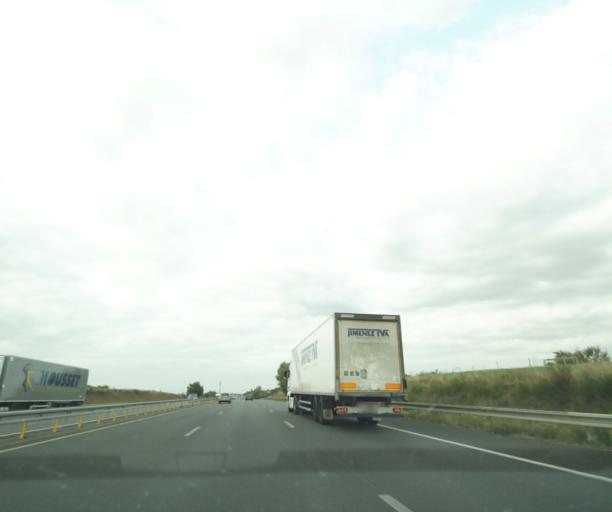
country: FR
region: Centre
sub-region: Departement d'Indre-et-Loire
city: Parcay-Meslay
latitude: 47.4327
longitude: 0.7359
